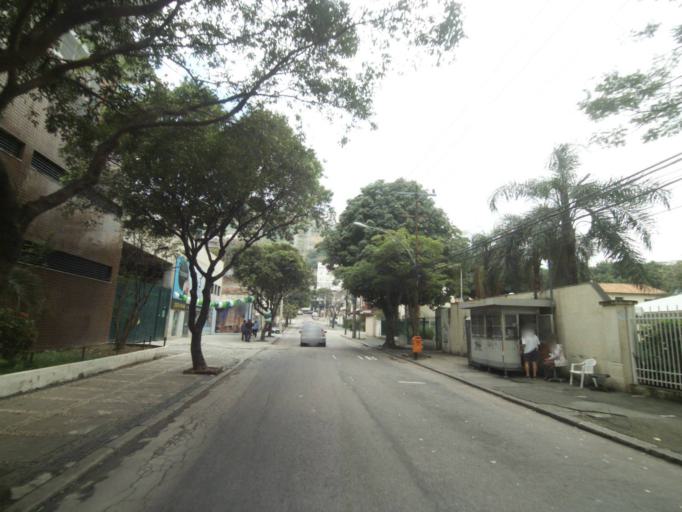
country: BR
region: Rio de Janeiro
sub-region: Rio De Janeiro
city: Rio de Janeiro
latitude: -22.9321
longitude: -43.2471
